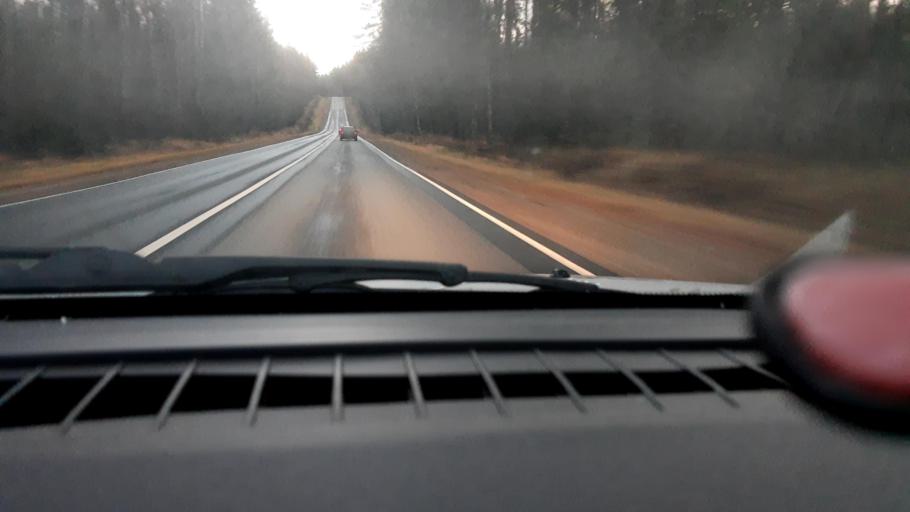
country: RU
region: Nizjnij Novgorod
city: Krasnyye Baki
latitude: 56.9979
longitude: 45.1135
